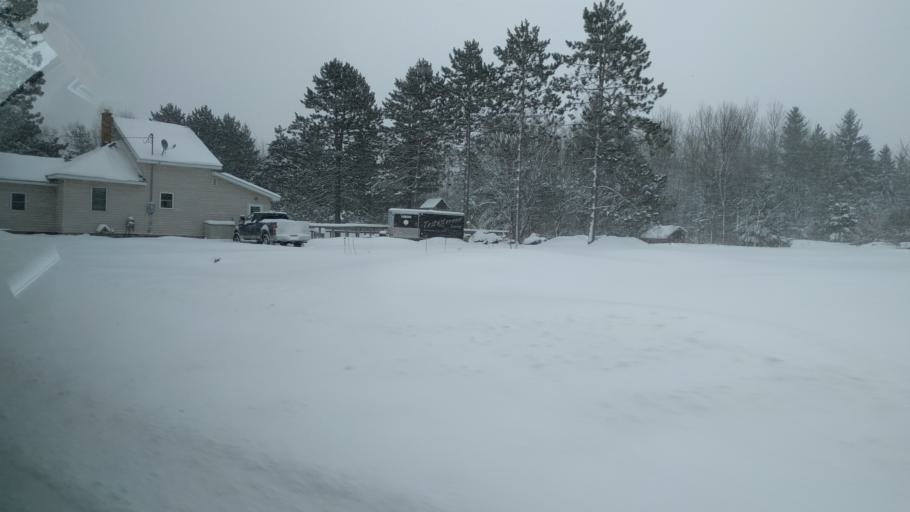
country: US
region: Wisconsin
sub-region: Iron County
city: Hurley
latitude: 46.4367
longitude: -90.2176
